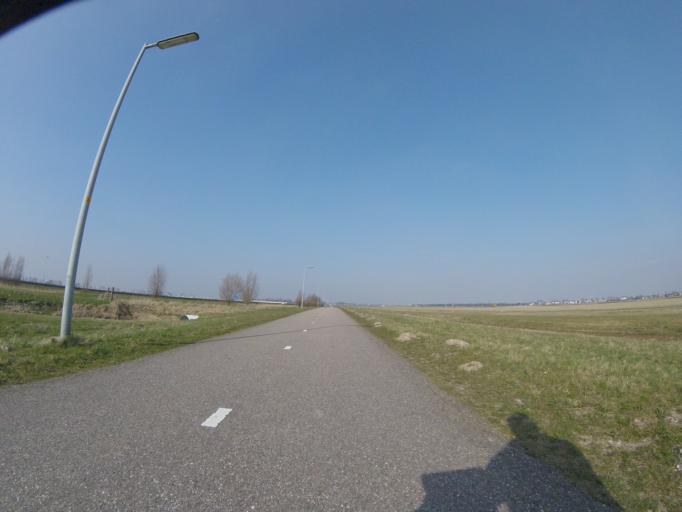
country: NL
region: North Holland
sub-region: Gemeente Haarlemmermeer
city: Hoofddorp
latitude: 52.3579
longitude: 4.7088
